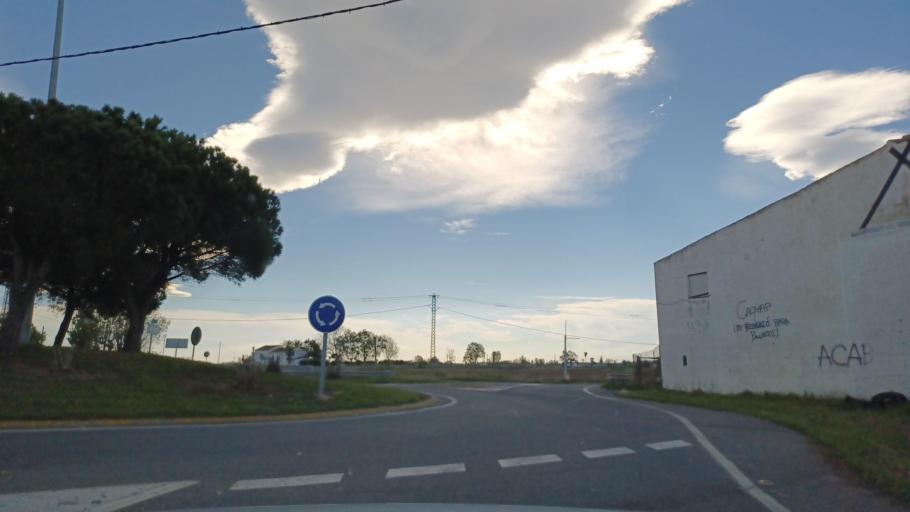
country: ES
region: Catalonia
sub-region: Provincia de Tarragona
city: Deltebre
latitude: 40.7298
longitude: 0.7103
